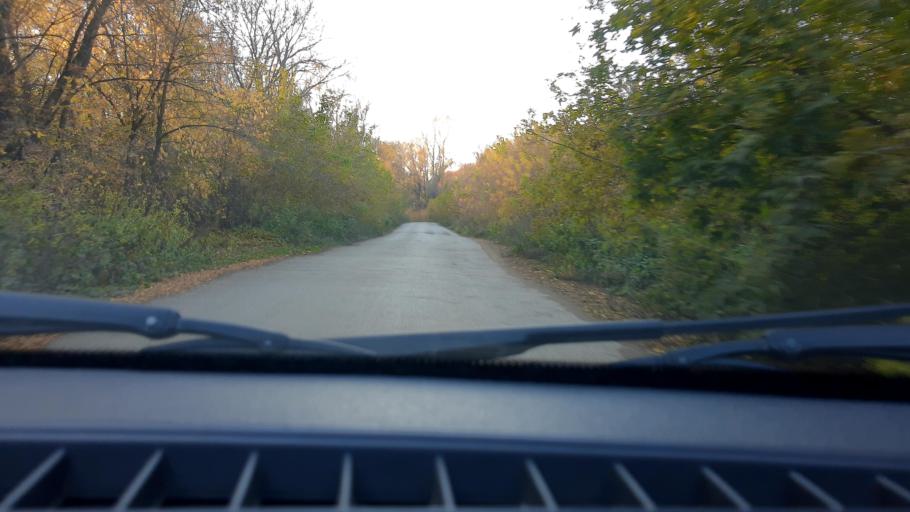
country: RU
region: Bashkortostan
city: Ufa
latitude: 54.7982
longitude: 56.1777
